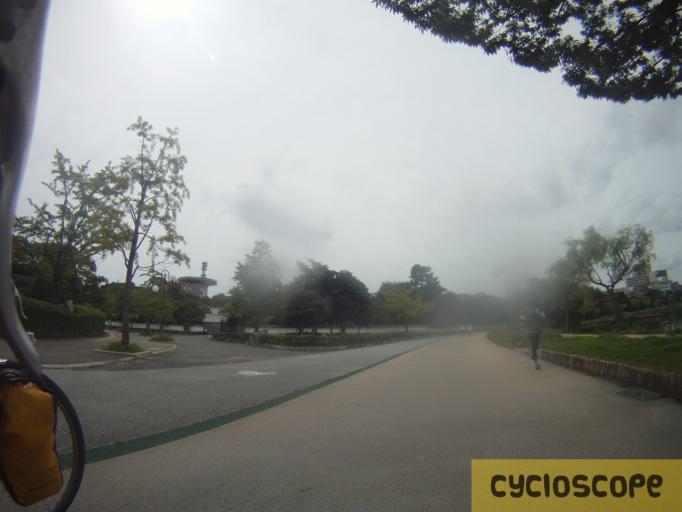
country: JP
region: Fukuoka
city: Fukuoka-shi
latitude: 33.5834
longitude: 130.3784
